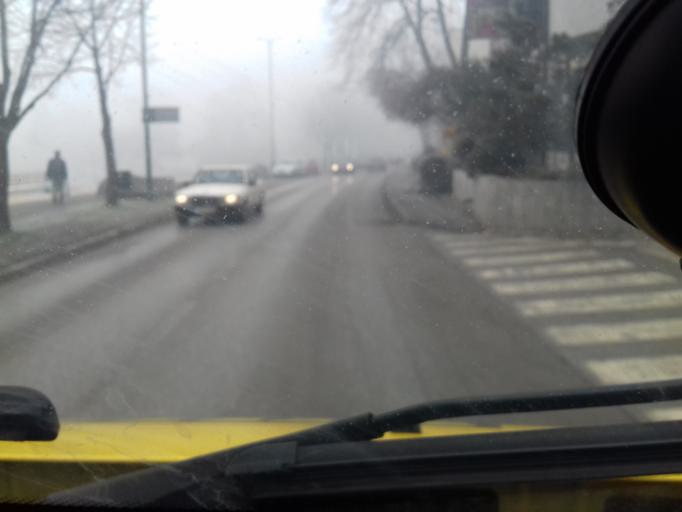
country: BA
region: Federation of Bosnia and Herzegovina
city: Visoko
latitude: 43.9945
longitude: 18.1738
